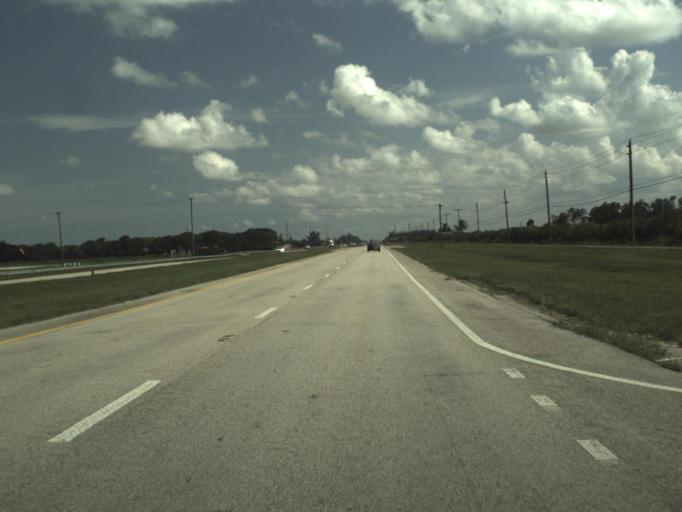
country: US
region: Florida
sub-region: Palm Beach County
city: Villages of Oriole
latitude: 26.5094
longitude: -80.2053
